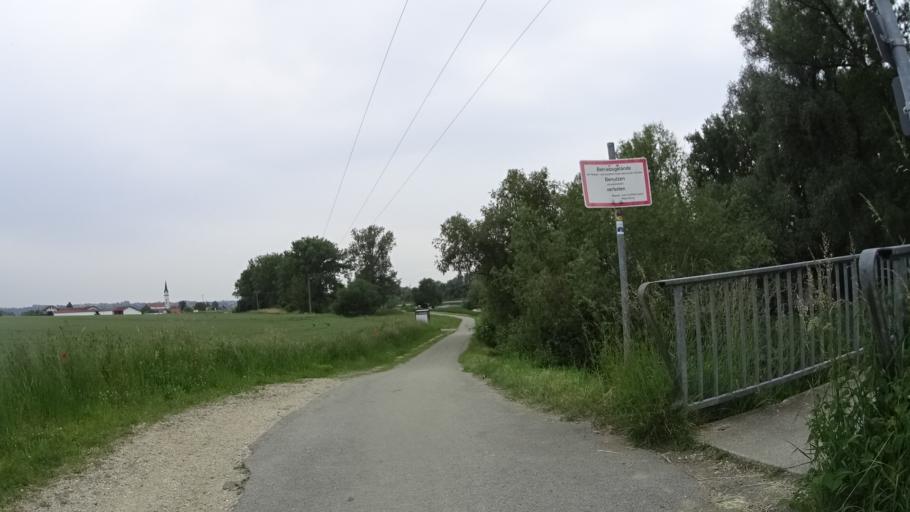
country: DE
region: Bavaria
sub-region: Lower Bavaria
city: Hofkirchen
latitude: 48.6874
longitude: 13.1139
